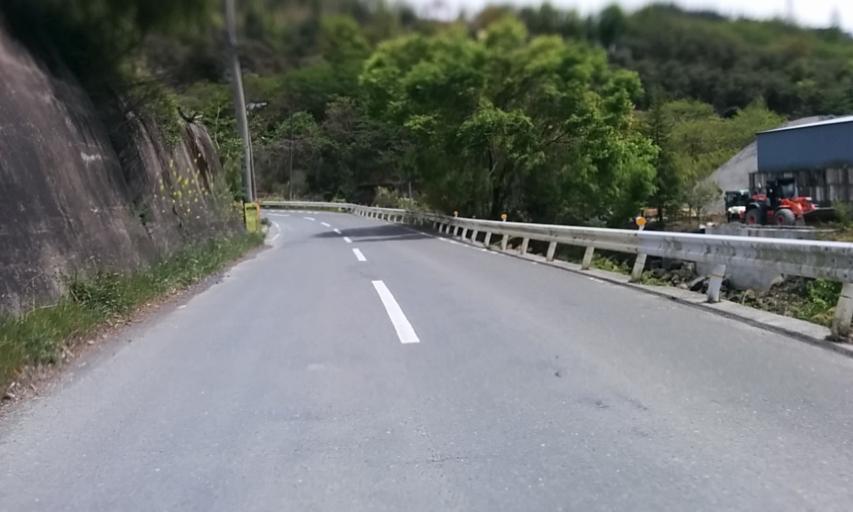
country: JP
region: Osaka
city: Takatsuki
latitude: 34.9150
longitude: 135.5997
